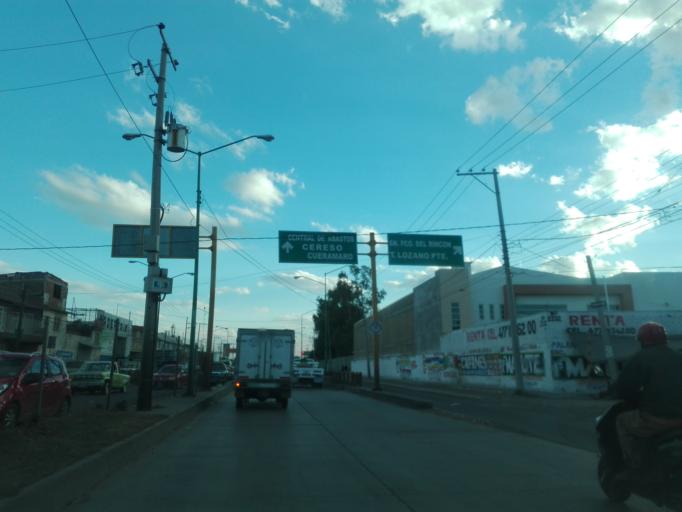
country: MX
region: Guanajuato
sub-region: Leon
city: San Jose de Duran (Los Troncoso)
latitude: 21.0932
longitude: -101.6794
